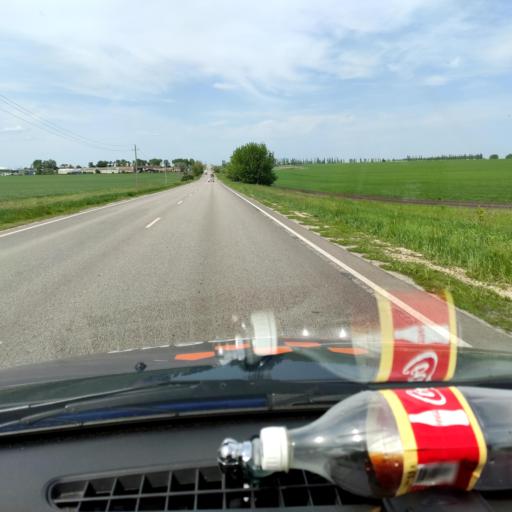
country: RU
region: Voronezj
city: Novaya Usman'
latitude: 51.5735
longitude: 39.3753
